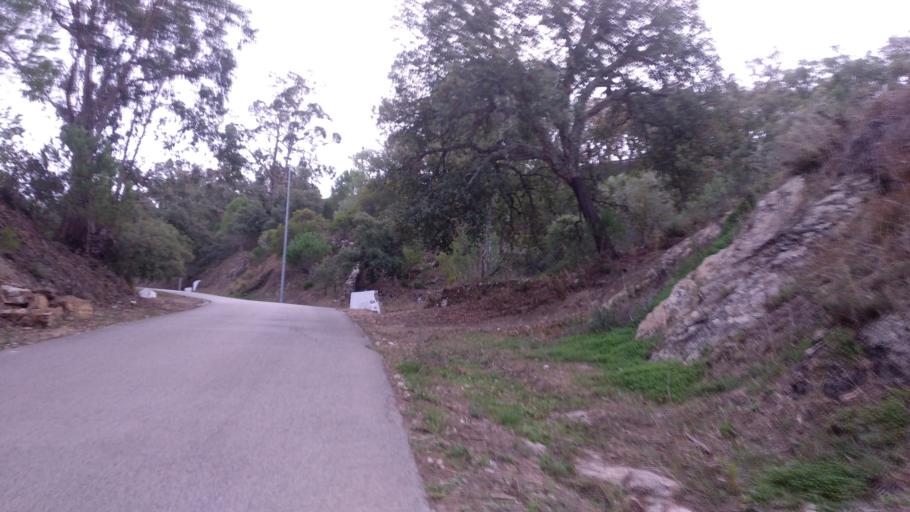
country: PT
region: Faro
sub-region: Sao Bras de Alportel
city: Sao Bras de Alportel
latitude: 37.1811
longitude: -7.9128
